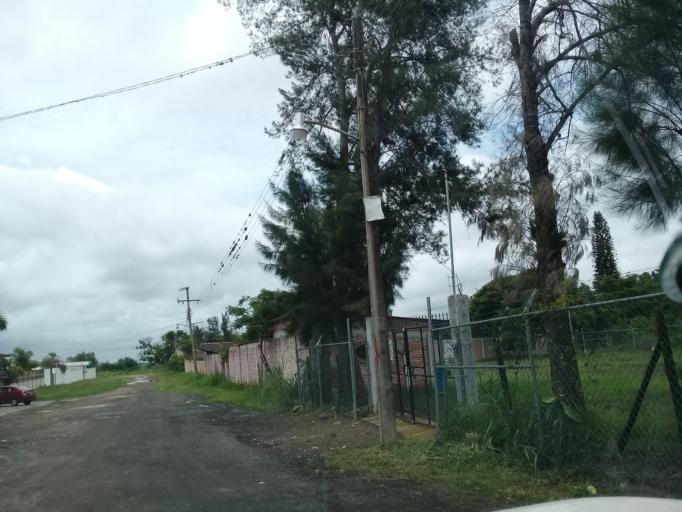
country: MX
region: Veracruz
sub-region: Emiliano Zapata
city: Dos Rios
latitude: 19.4818
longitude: -96.7919
